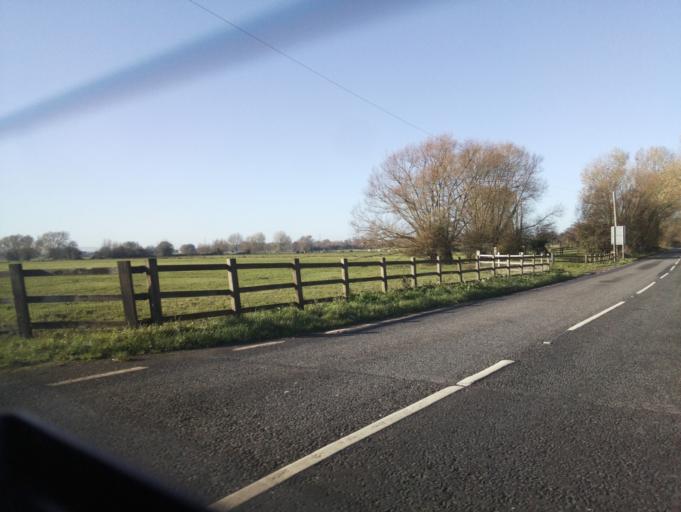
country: GB
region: England
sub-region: Somerset
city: Curry Rivel
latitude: 51.0800
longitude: -2.8700
